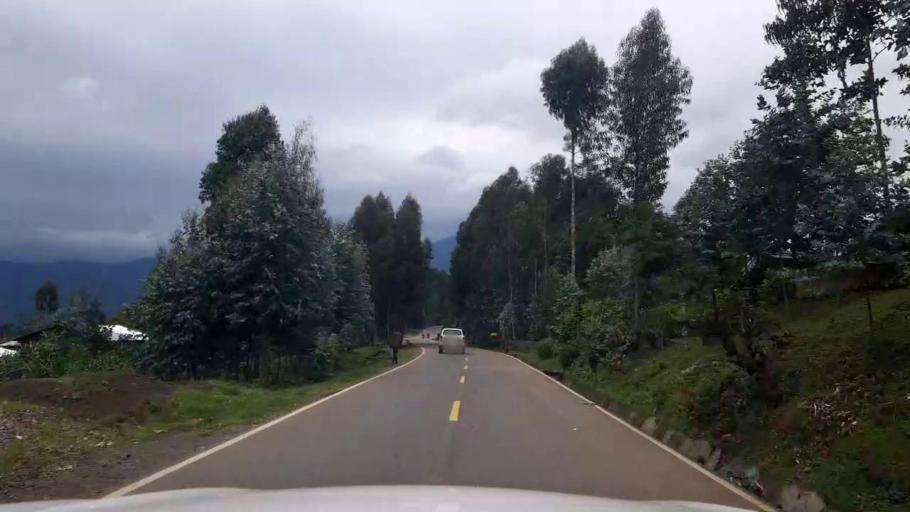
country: RW
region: Northern Province
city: Musanze
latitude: -1.4392
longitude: 29.5448
